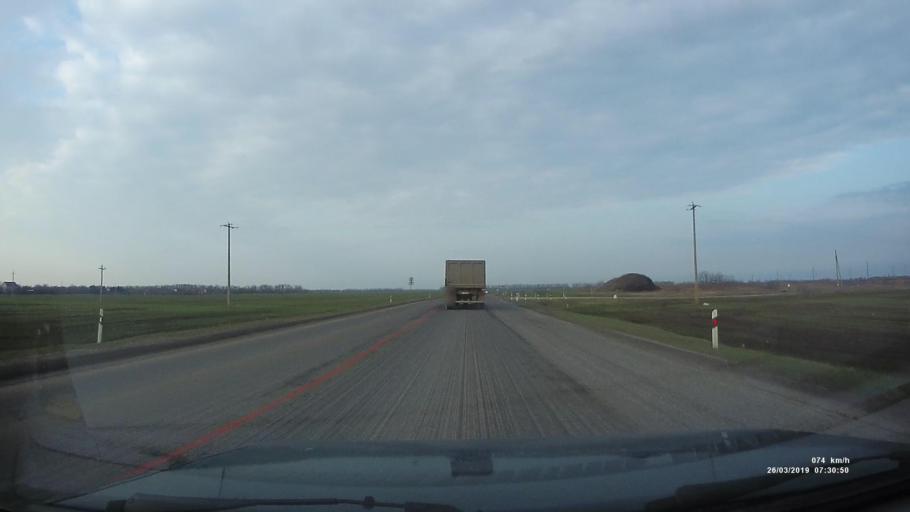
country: RU
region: Rostov
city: Novobessergenovka
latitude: 47.2349
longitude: 38.8006
